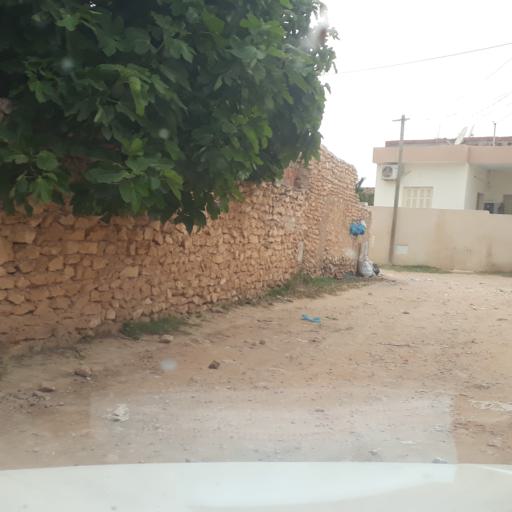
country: TN
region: Safaqis
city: Al Qarmadah
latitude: 34.8242
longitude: 10.7776
